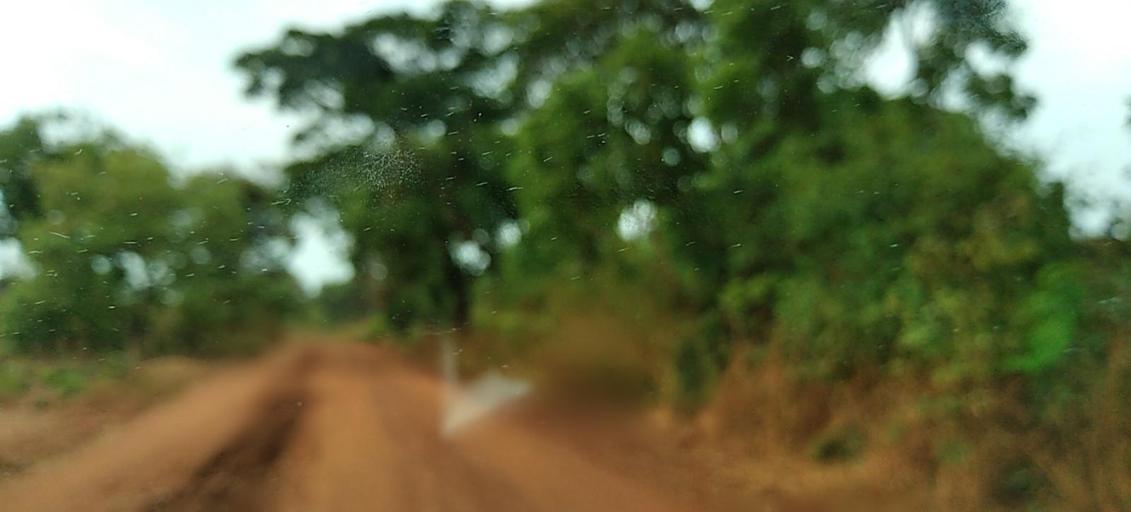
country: ZM
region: North-Western
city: Solwezi
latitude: -12.2485
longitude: 26.5129
